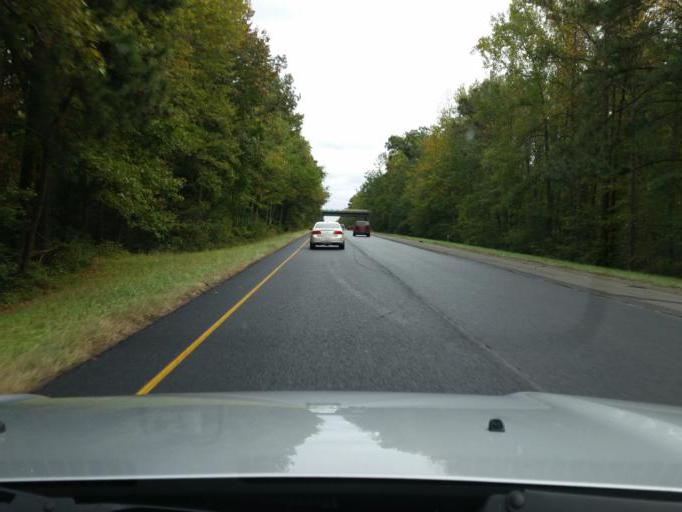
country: US
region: Virginia
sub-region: Henrico County
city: Sandston
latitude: 37.5126
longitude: -77.1642
